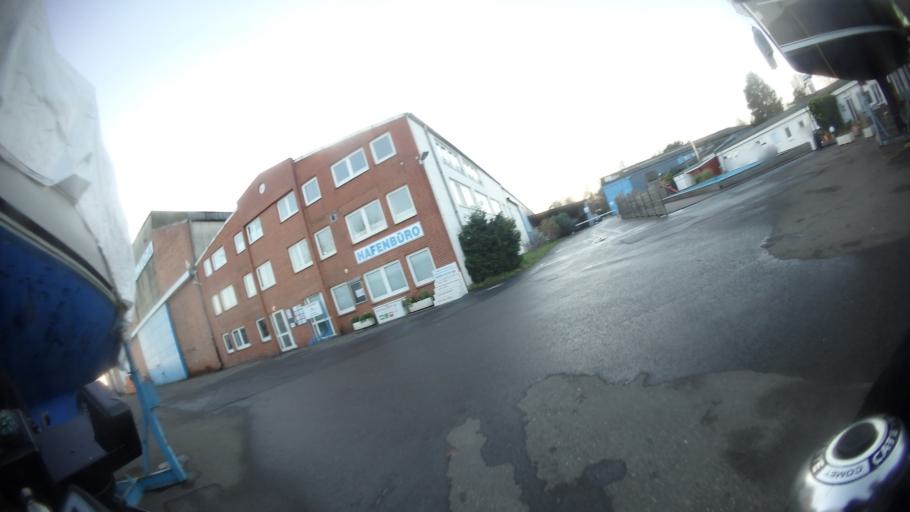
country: DE
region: Schleswig-Holstein
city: Travemuende
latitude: 53.9527
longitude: 10.8567
